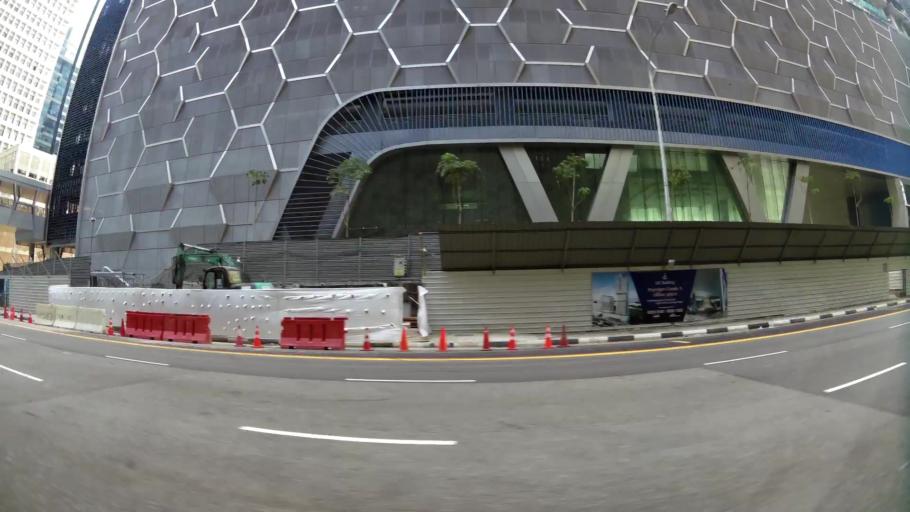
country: SG
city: Singapore
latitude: 1.2778
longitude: 103.8495
